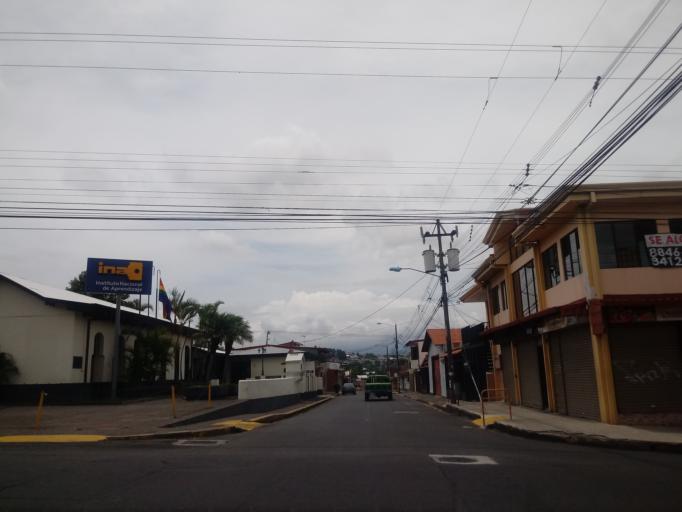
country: CR
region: Heredia
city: Heredia
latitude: 10.0012
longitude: -84.1143
